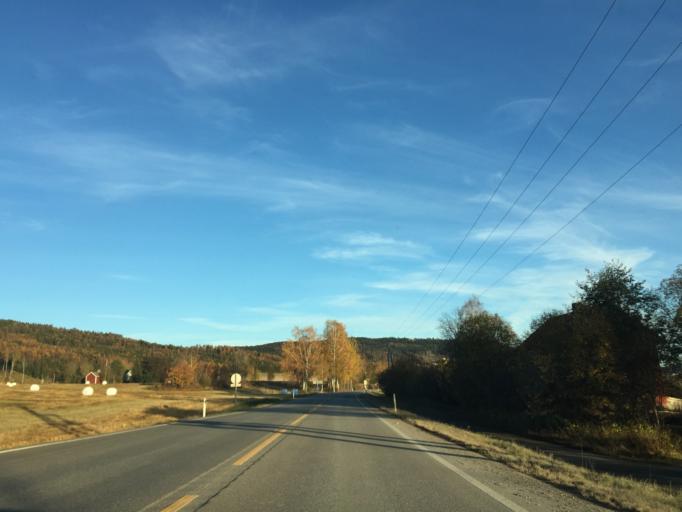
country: NO
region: Hedmark
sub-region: Kongsvinger
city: Spetalen
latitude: 60.2151
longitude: 11.9346
